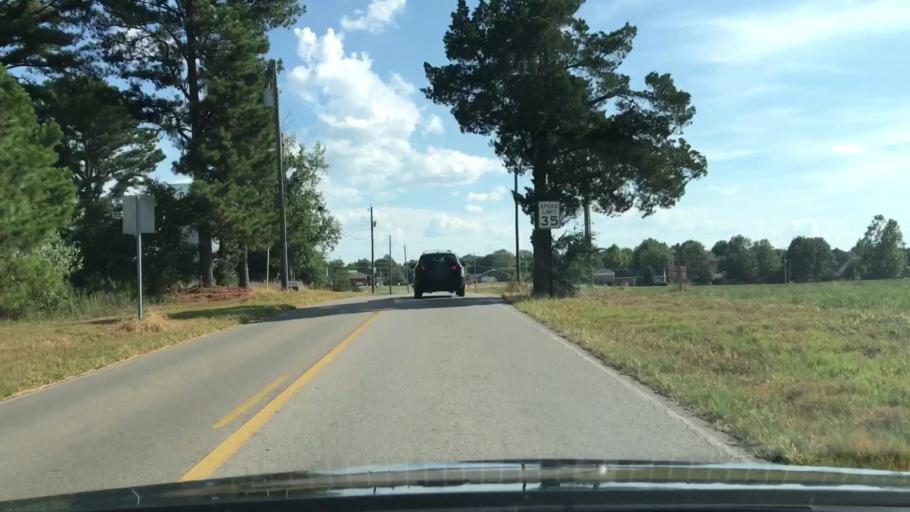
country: US
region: Alabama
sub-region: Madison County
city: Harvest
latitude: 34.8624
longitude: -86.7491
